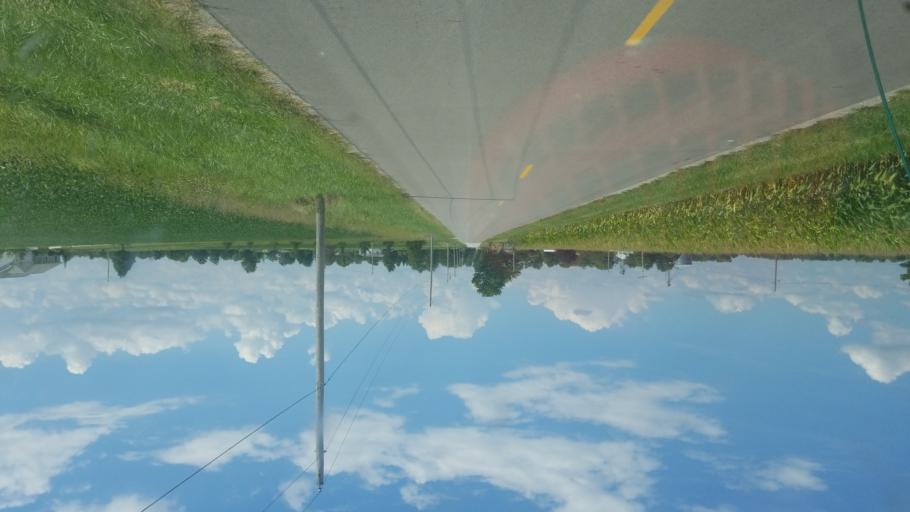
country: US
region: Ohio
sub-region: Hardin County
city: Forest
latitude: 40.8613
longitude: -83.4740
